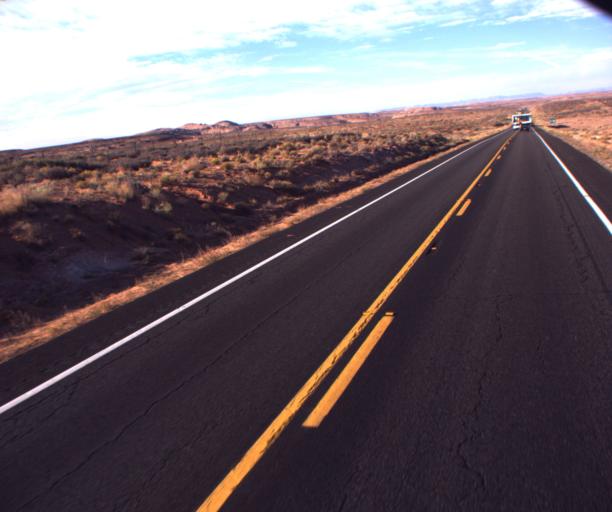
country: US
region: Arizona
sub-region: Apache County
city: Many Farms
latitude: 36.9342
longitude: -109.5640
